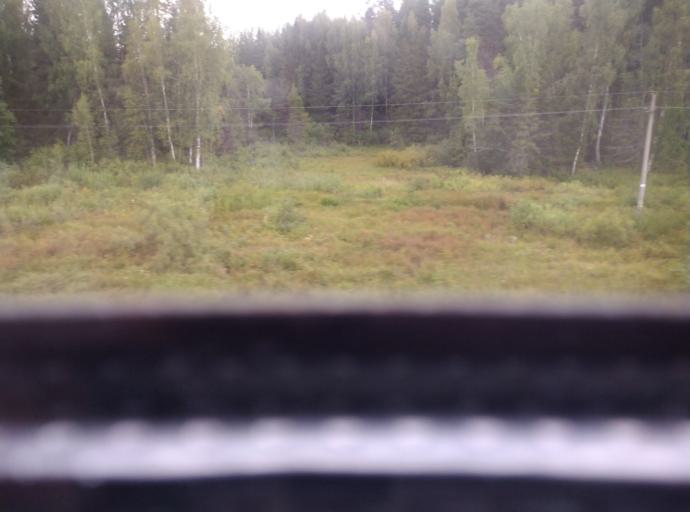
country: RU
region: Jaroslavl
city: Burmakino
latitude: 57.4366
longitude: 40.3414
